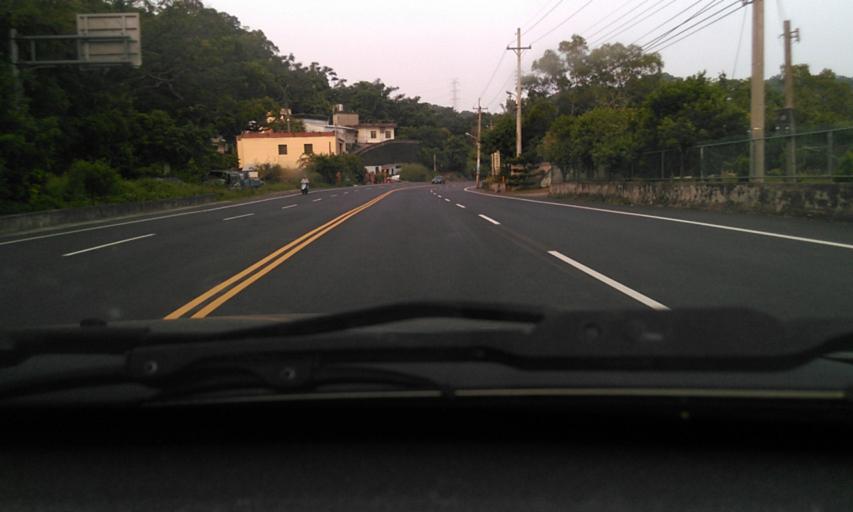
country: TW
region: Taiwan
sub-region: Hsinchu
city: Hsinchu
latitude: 24.6877
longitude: 120.9687
